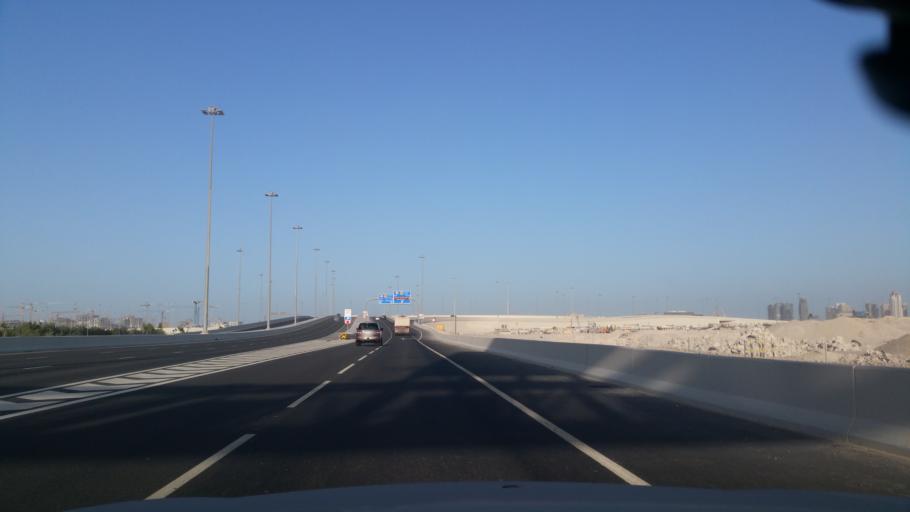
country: QA
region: Baladiyat Umm Salal
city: Umm Salal Muhammad
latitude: 25.4011
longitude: 51.4844
